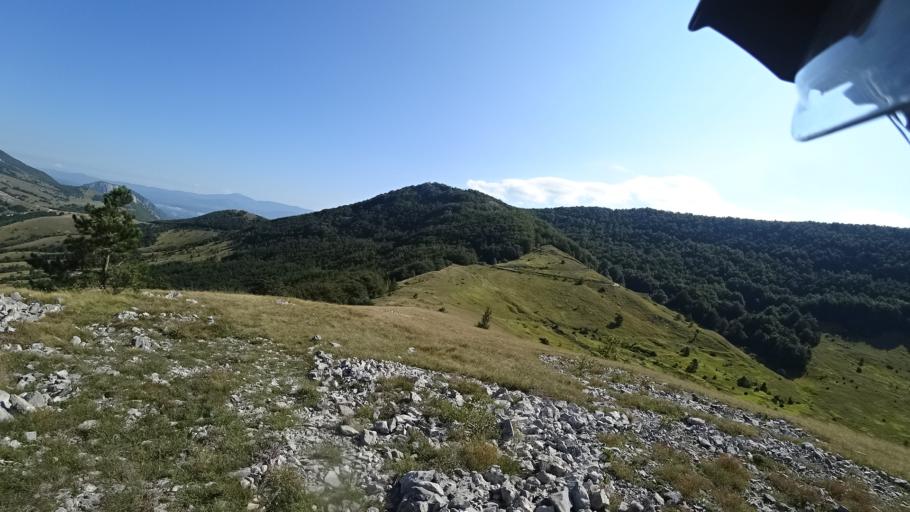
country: HR
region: Zadarska
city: Gracac
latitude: 44.2806
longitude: 16.0866
